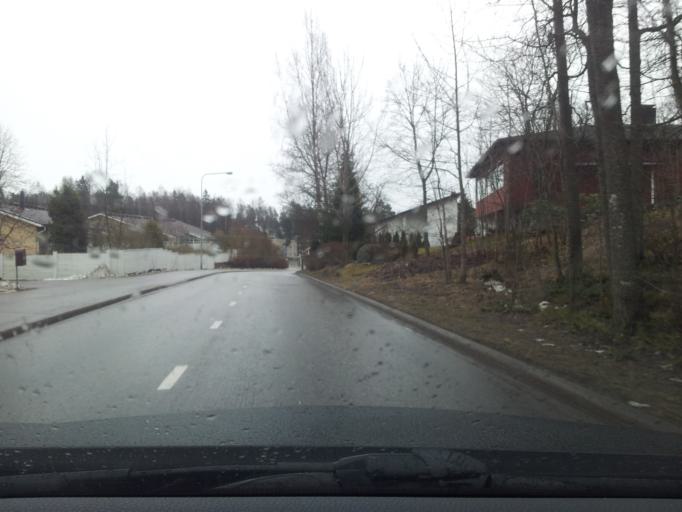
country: FI
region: Uusimaa
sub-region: Helsinki
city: Espoo
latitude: 60.1618
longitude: 24.6778
